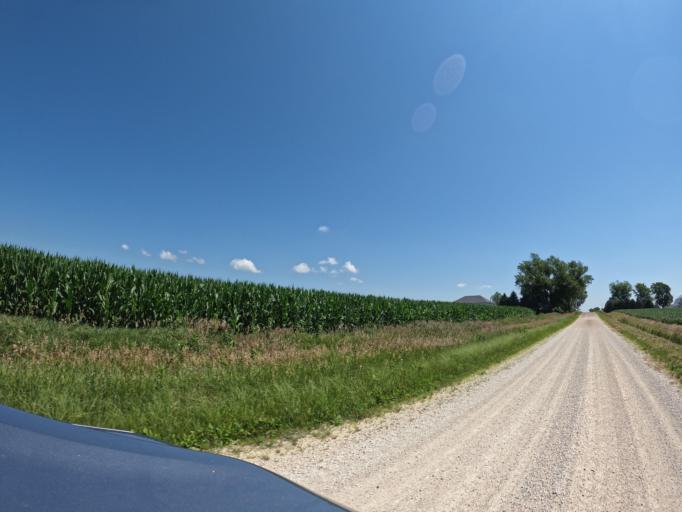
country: US
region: Iowa
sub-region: Clinton County
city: De Witt
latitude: 41.7720
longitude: -90.4022
